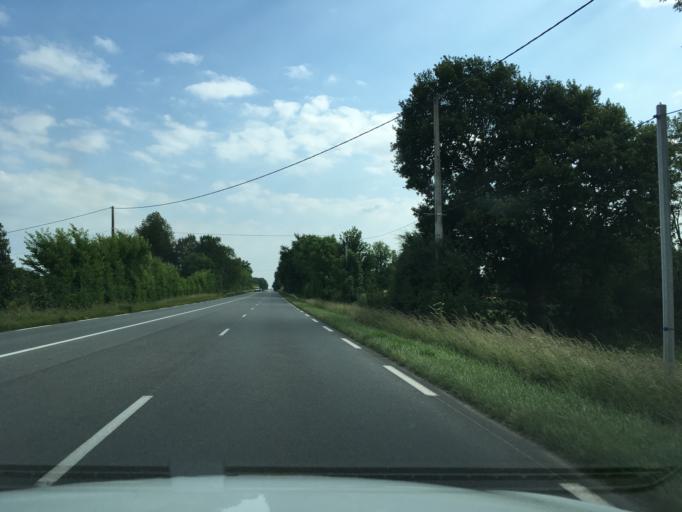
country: FR
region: Poitou-Charentes
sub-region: Departement des Deux-Sevres
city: Le Tallud
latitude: 46.6086
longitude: -0.2858
